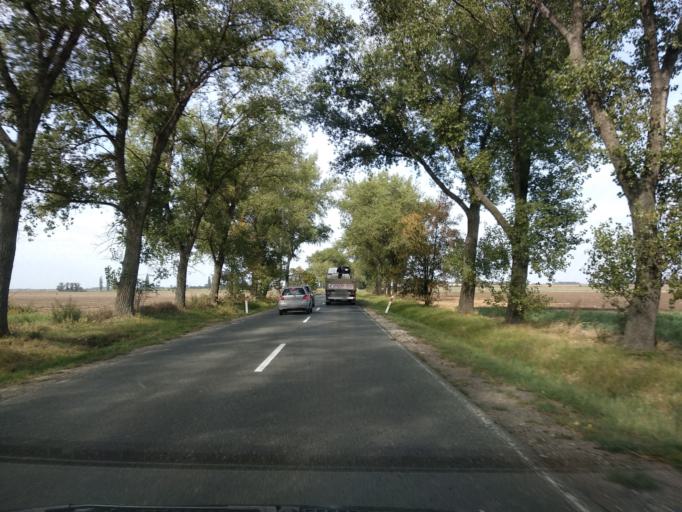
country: PL
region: Lower Silesian Voivodeship
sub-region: Powiat strzelinski
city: Strzelin
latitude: 50.8787
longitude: 17.0628
